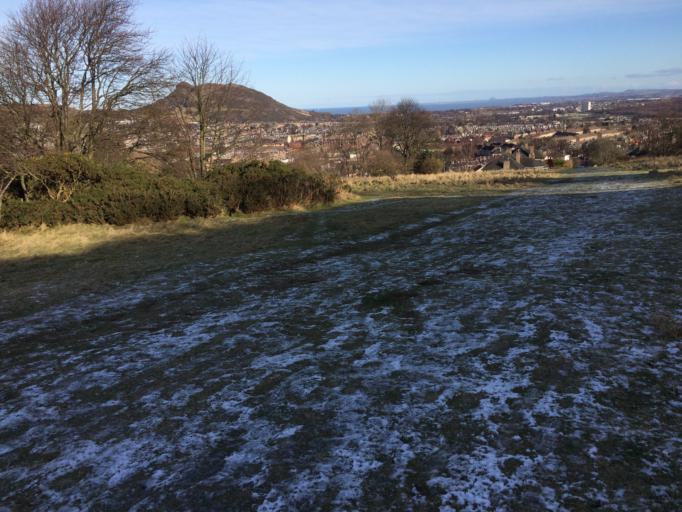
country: GB
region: Scotland
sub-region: Edinburgh
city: Edinburgh
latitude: 55.9236
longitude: -3.1885
